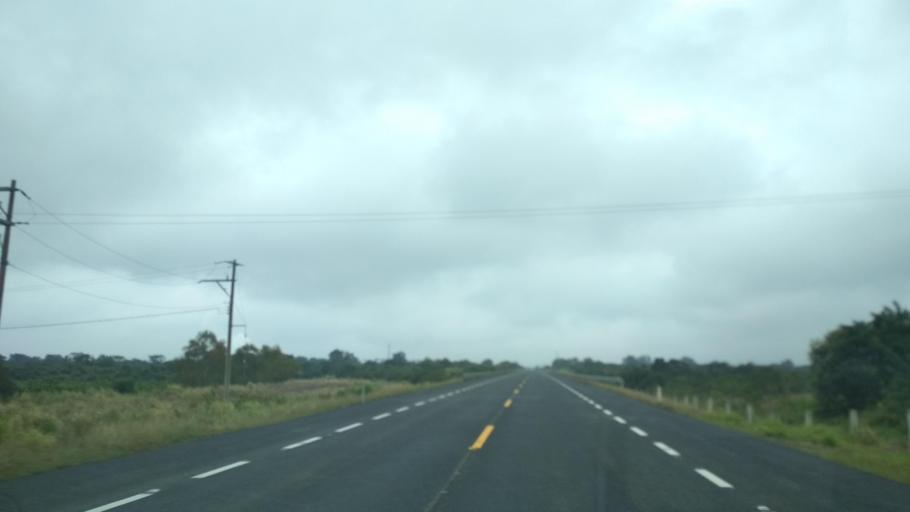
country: MX
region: Veracruz
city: Vega de San Marcos
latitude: 20.1661
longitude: -96.9573
